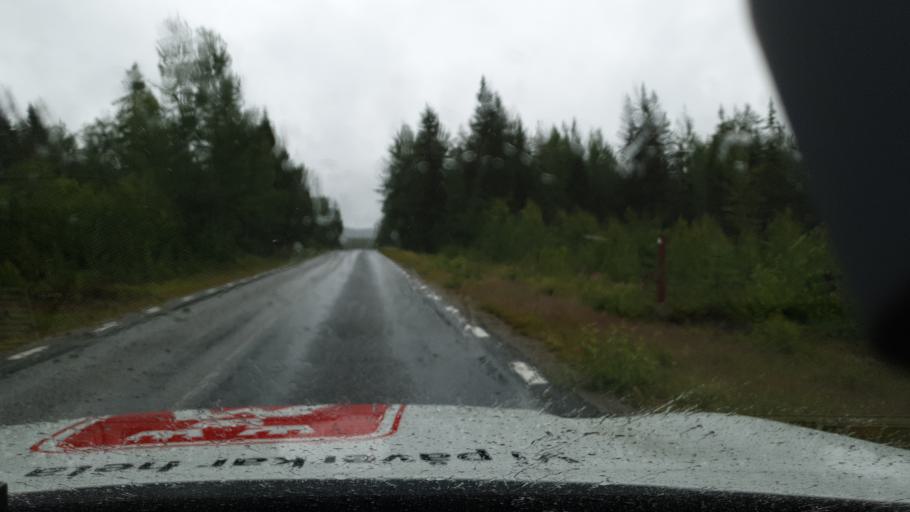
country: SE
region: Vaesterbotten
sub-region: Asele Kommun
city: Insjon
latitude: 64.3304
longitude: 17.7348
